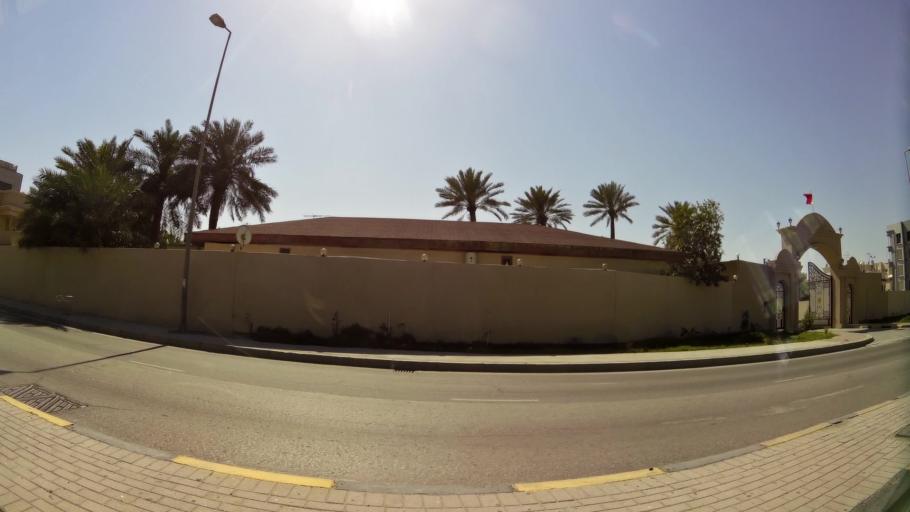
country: BH
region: Manama
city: Manama
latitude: 26.2135
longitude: 50.5822
